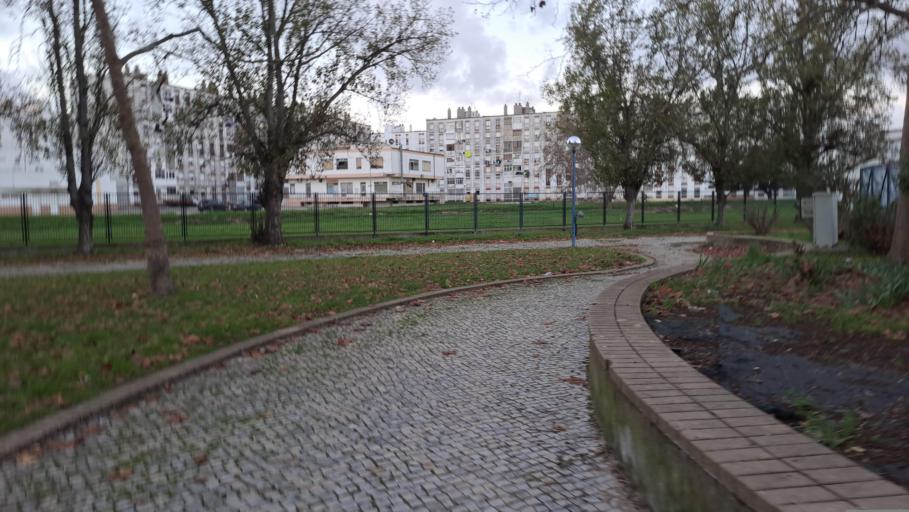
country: PT
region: Setubal
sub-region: Moita
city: Alhos Vedros
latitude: 38.6496
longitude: -9.0371
